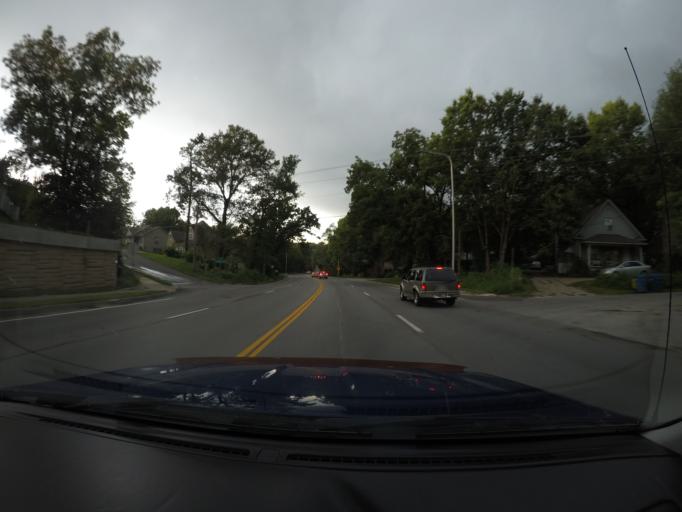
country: US
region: Missouri
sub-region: Jackson County
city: Sugar Creek
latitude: 39.1018
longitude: -94.4617
